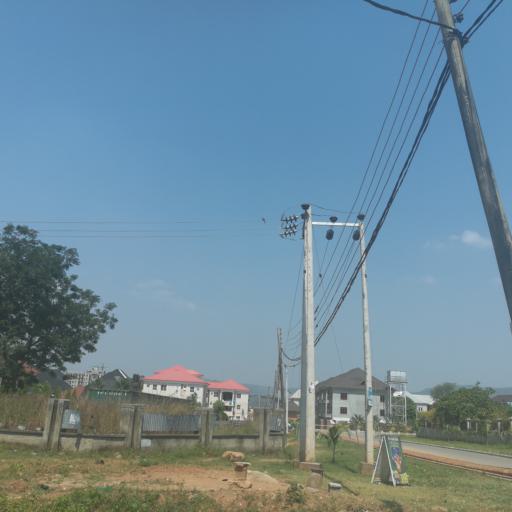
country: NG
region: Abuja Federal Capital Territory
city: Abuja
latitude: 9.0829
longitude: 7.4470
